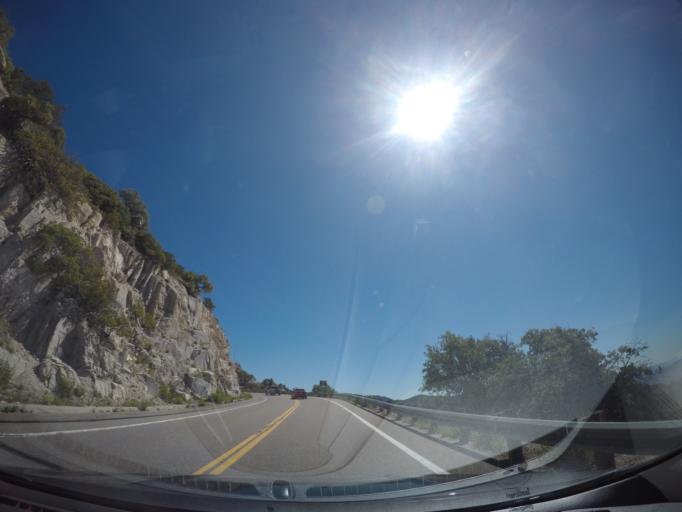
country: US
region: Arizona
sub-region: Pima County
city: Tanque Verde
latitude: 32.3754
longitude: -110.7032
